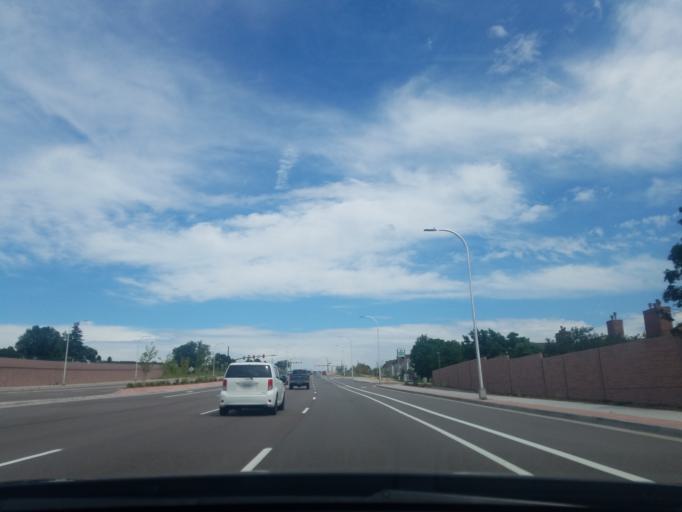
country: US
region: Colorado
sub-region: El Paso County
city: Air Force Academy
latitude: 38.9330
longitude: -104.7796
